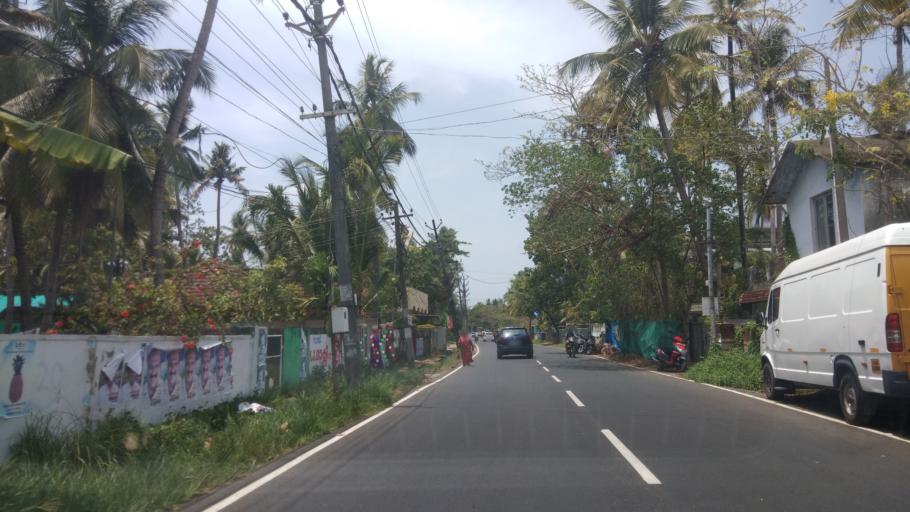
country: IN
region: Kerala
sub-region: Ernakulam
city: Cochin
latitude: 9.8990
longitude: 76.2576
